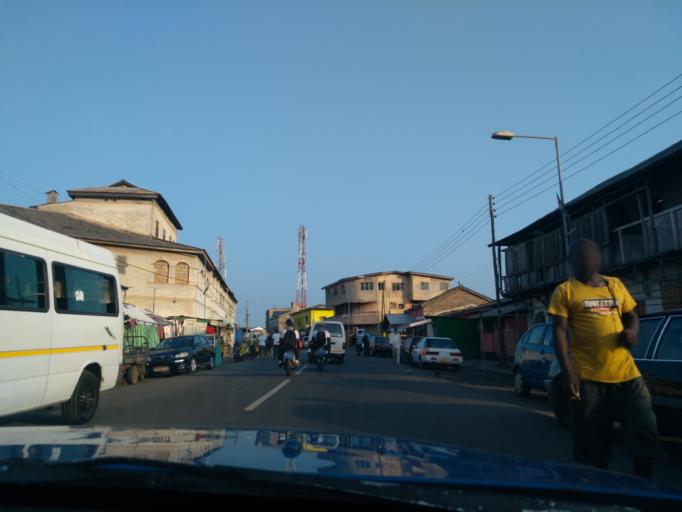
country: GH
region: Greater Accra
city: Accra
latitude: 5.5377
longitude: -0.2128
